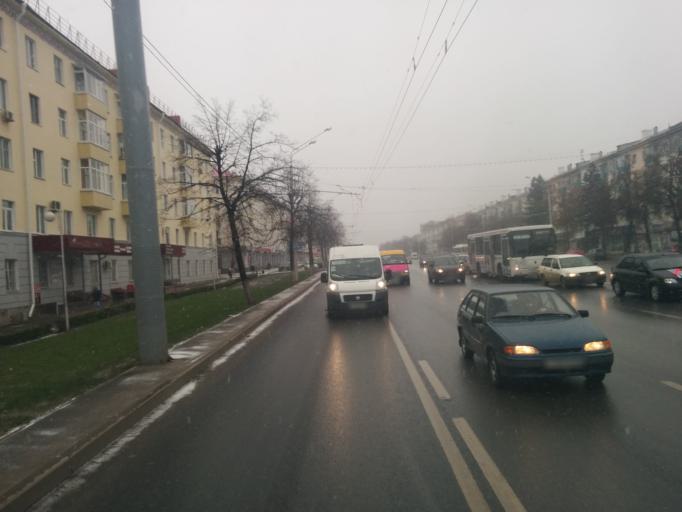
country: RU
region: Bashkortostan
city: Ufa
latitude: 54.7449
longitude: 55.9915
